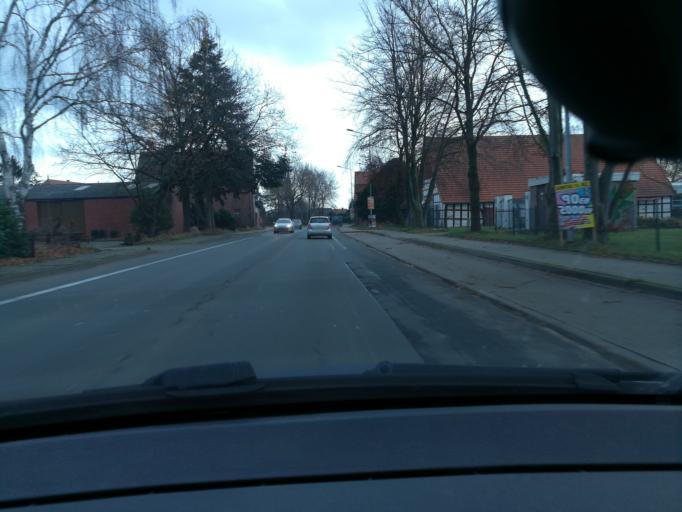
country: DE
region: North Rhine-Westphalia
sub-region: Regierungsbezirk Detmold
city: Hille
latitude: 52.3215
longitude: 8.7893
